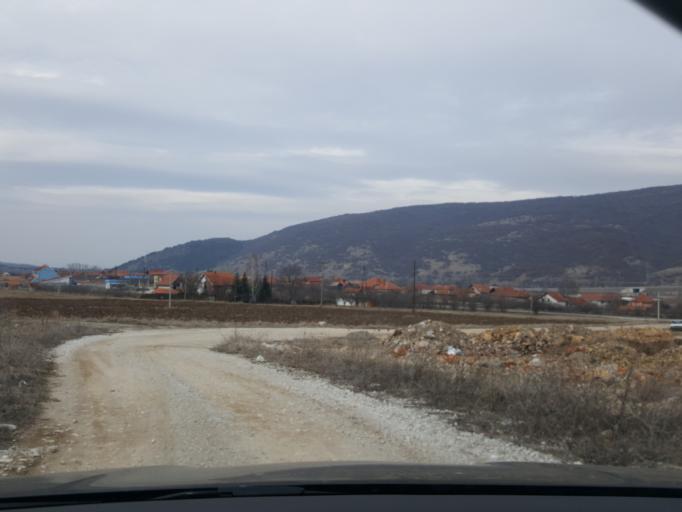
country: RS
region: Central Serbia
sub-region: Pirotski Okrug
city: Dimitrovgrad
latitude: 43.0094
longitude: 22.7466
